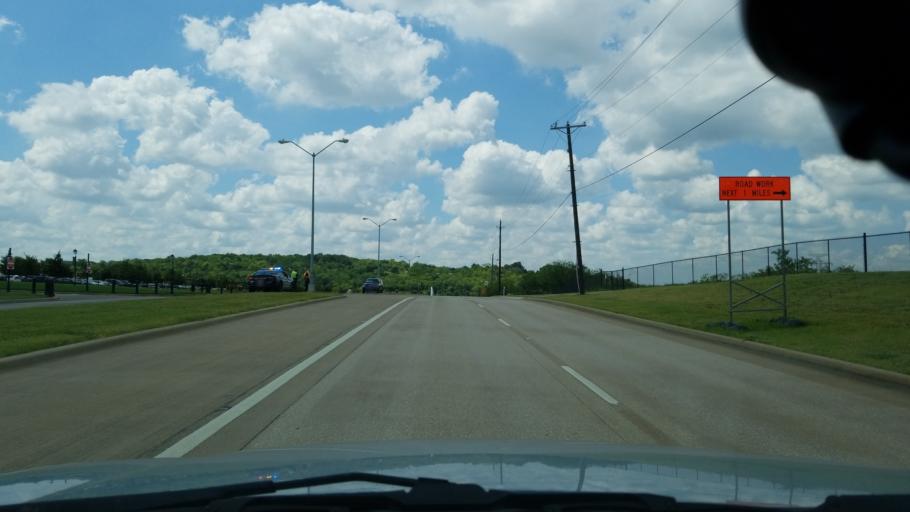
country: US
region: Texas
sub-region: Dallas County
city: Grand Prairie
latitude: 32.7108
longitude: -96.9517
